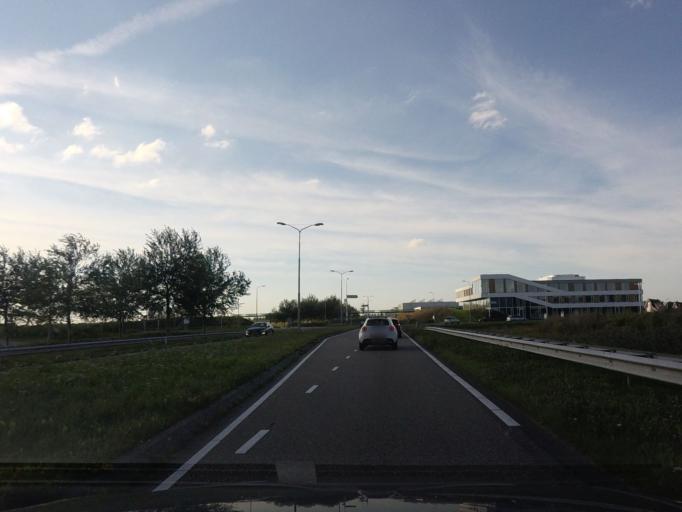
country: NL
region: North Holland
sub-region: Gemeente Bloemendaal
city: Bennebroek
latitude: 52.2982
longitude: 4.6355
